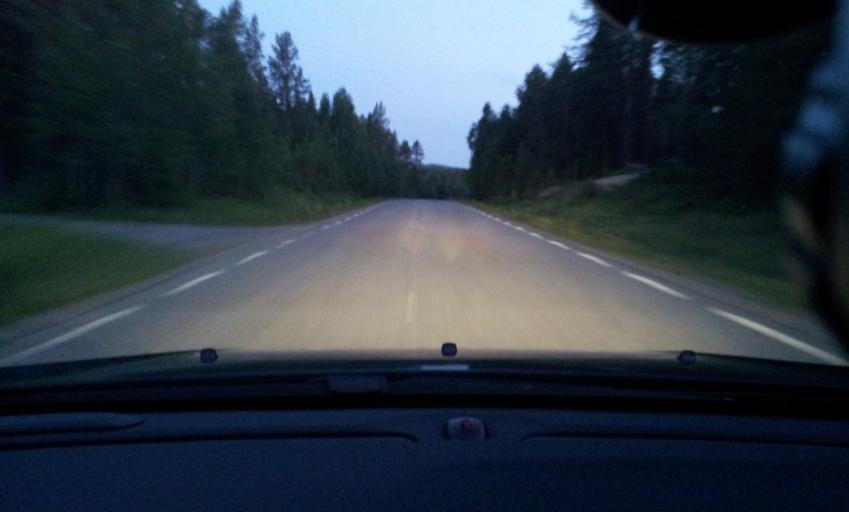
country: SE
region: Jaemtland
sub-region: Braecke Kommun
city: Braecke
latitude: 62.7436
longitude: 15.2151
